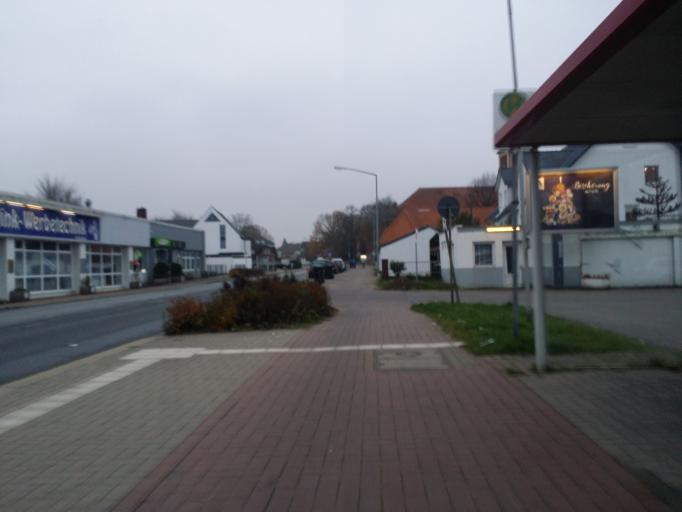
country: DE
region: Lower Saxony
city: Stuhr
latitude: 53.0170
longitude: 8.7894
